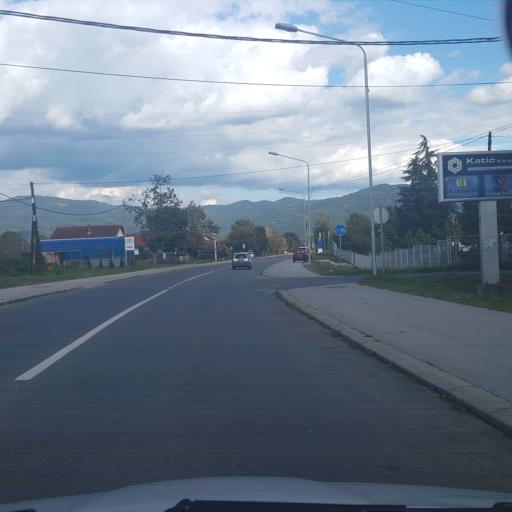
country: RS
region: Central Serbia
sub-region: Raski Okrug
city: Vrnjacka Banja
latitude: 43.6310
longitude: 20.9026
